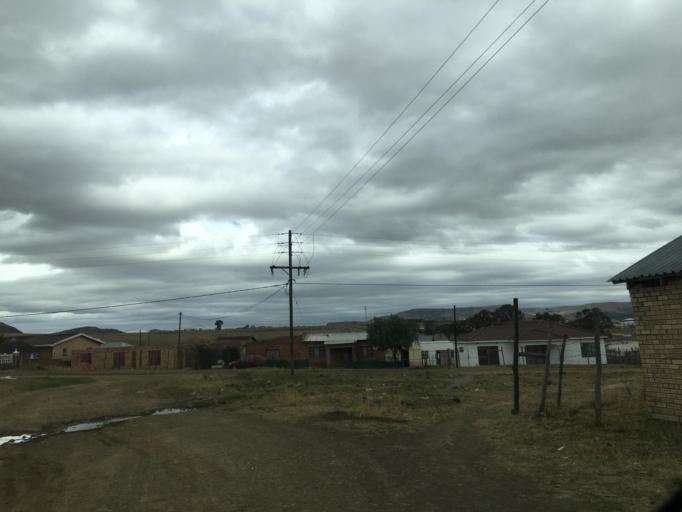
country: ZA
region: Eastern Cape
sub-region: Chris Hani District Municipality
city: Cala
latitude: -31.5376
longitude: 27.6907
